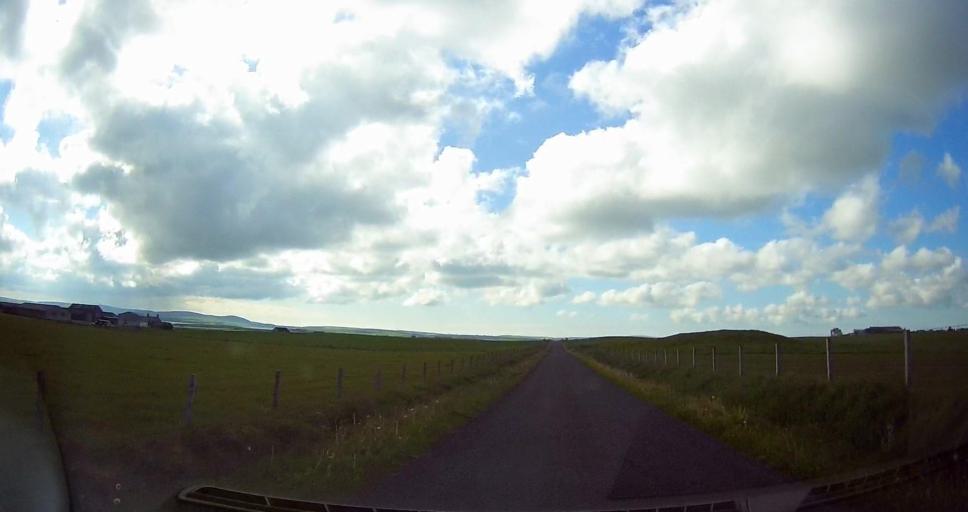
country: GB
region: Scotland
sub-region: Orkney Islands
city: Stromness
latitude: 58.9967
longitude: -3.1635
